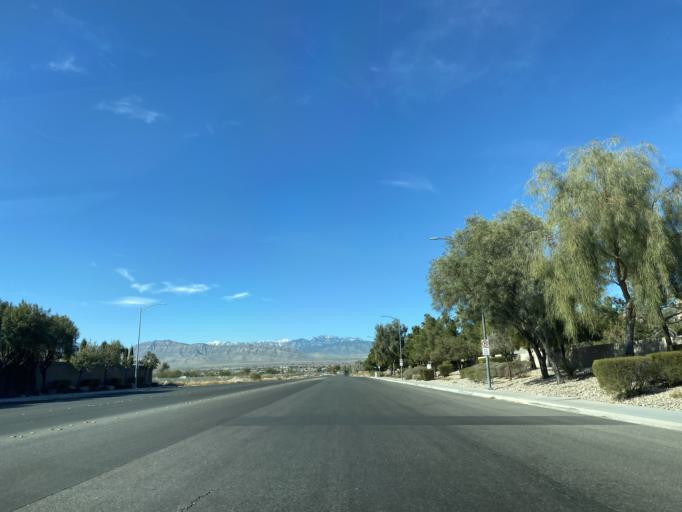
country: US
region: Nevada
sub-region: Clark County
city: North Las Vegas
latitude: 36.3052
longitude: -115.2379
